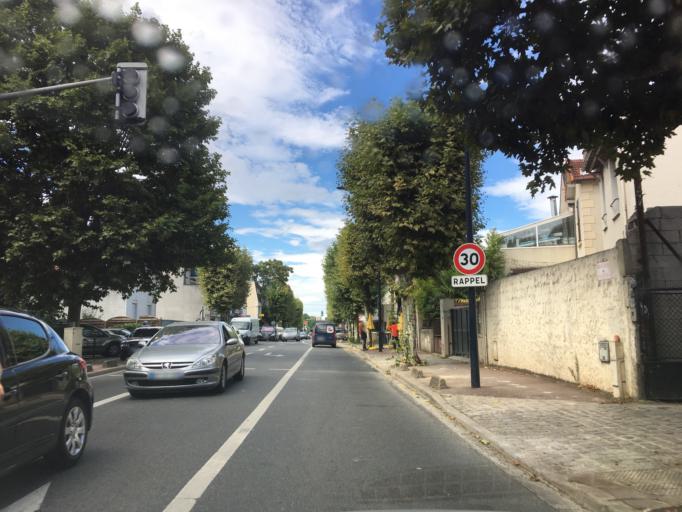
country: FR
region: Ile-de-France
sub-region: Departement du Val-de-Marne
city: Champigny-sur-Marne
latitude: 48.8199
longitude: 2.5112
